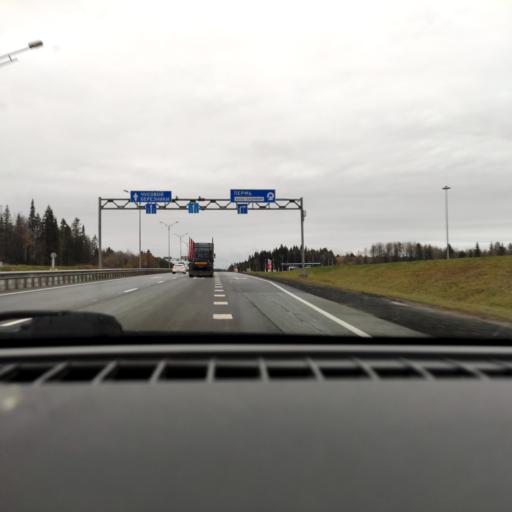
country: RU
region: Perm
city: Ferma
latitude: 57.9988
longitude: 56.3866
